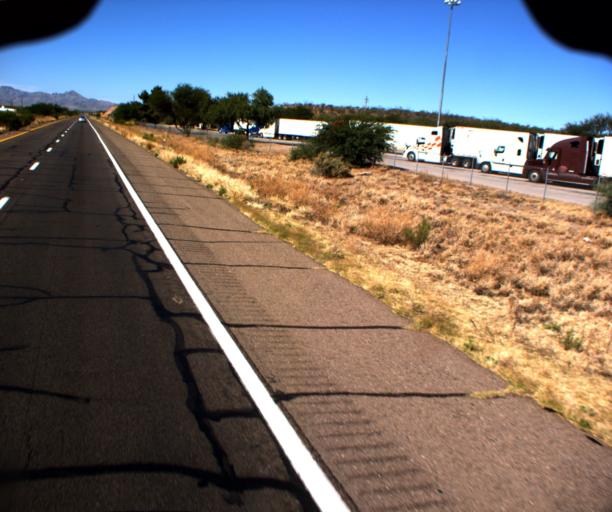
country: US
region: Arizona
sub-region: Pima County
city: Arivaca Junction
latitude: 31.7713
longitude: -111.0332
